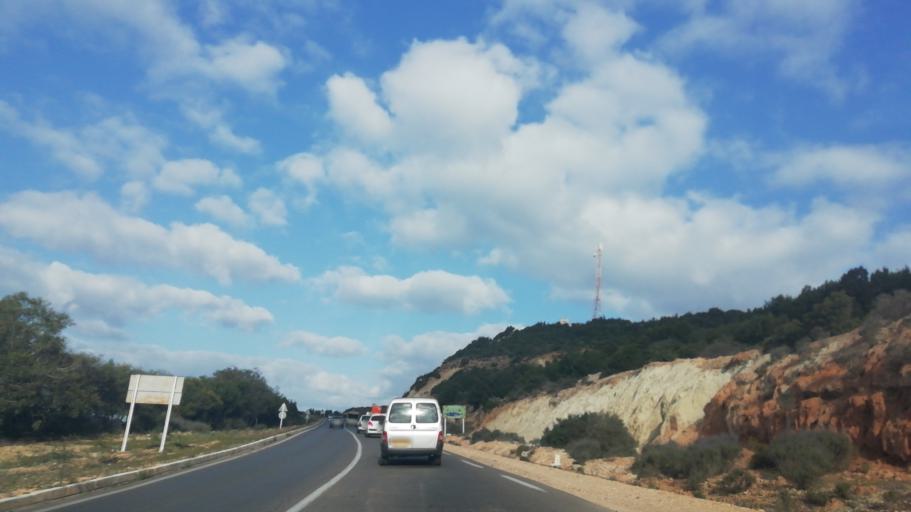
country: DZ
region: Relizane
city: Mazouna
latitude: 36.2395
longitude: 0.5422
